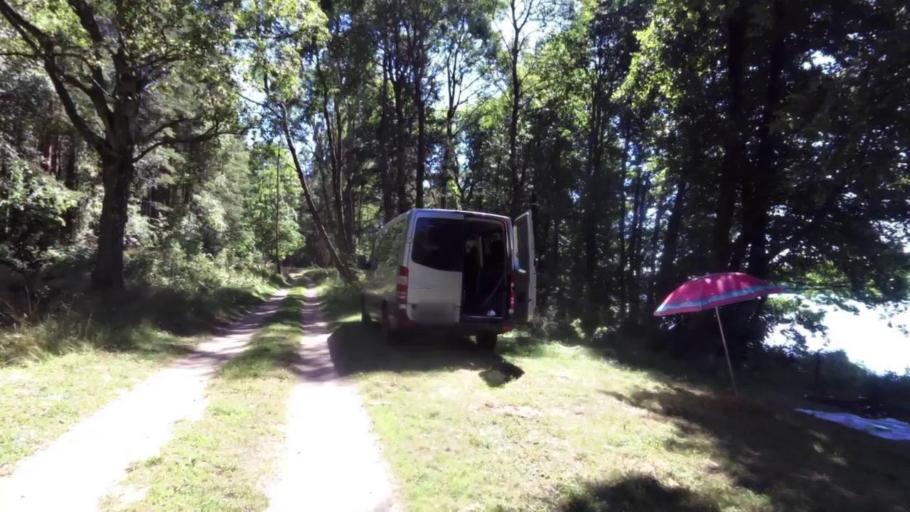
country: PL
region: West Pomeranian Voivodeship
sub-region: Powiat szczecinecki
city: Bialy Bor
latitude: 53.8497
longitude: 16.8703
